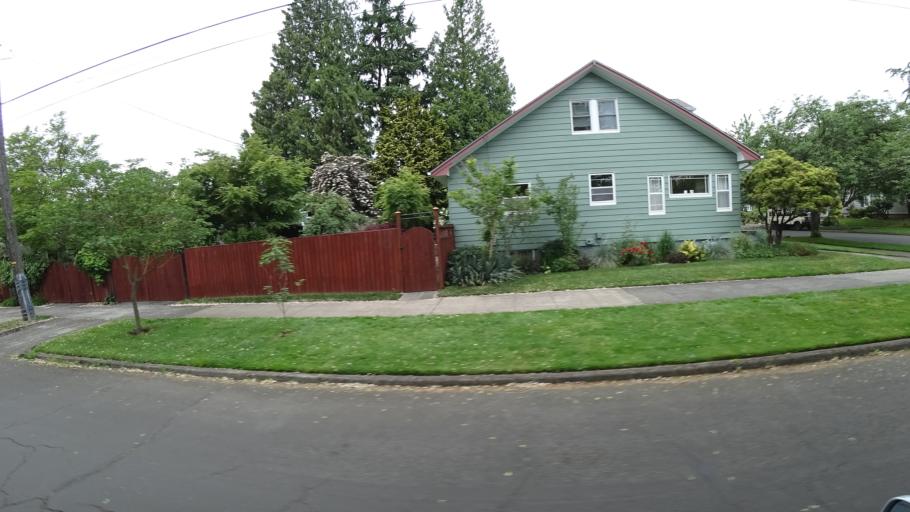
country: US
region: Oregon
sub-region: Multnomah County
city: Portland
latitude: 45.5454
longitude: -122.6161
